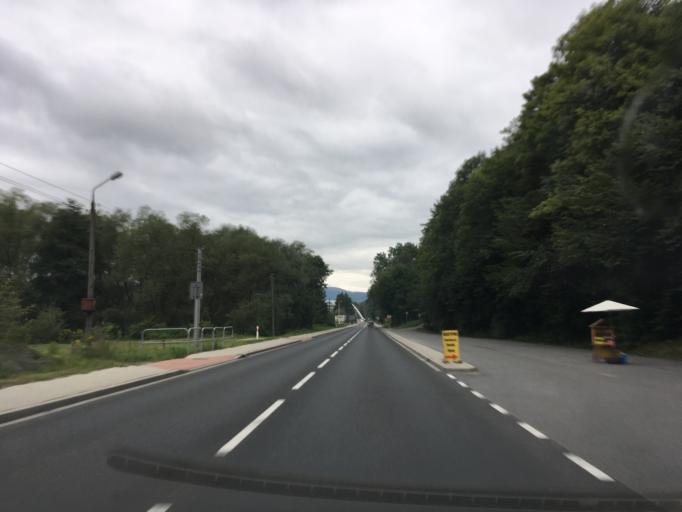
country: PL
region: Lesser Poland Voivodeship
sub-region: Powiat suski
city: Sucha Beskidzka
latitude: 49.7367
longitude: 19.6160
